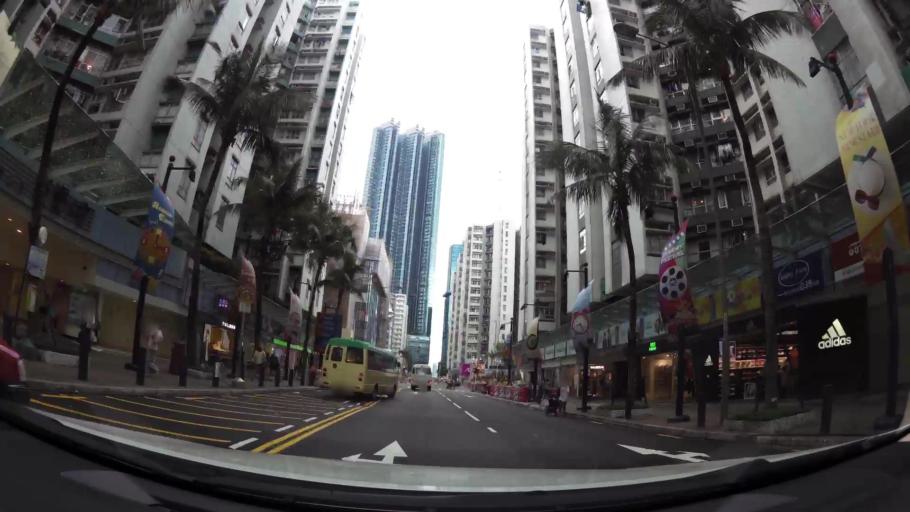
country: HK
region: Kowloon City
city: Kowloon
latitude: 22.3051
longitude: 114.1895
